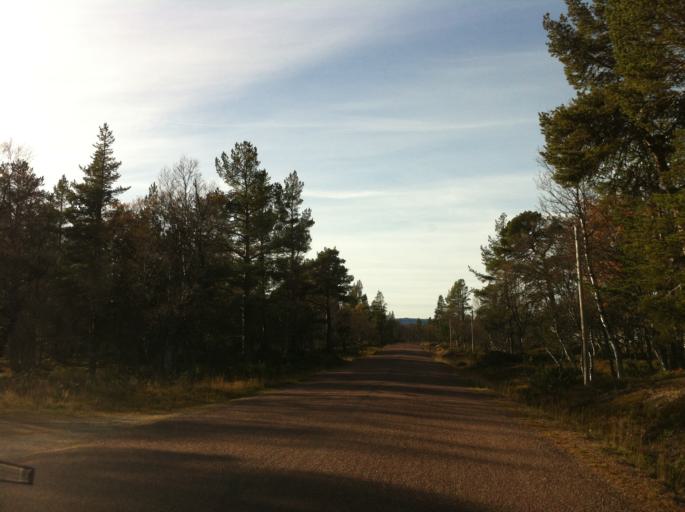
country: NO
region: Hedmark
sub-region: Engerdal
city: Engerdal
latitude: 62.0709
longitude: 12.2060
